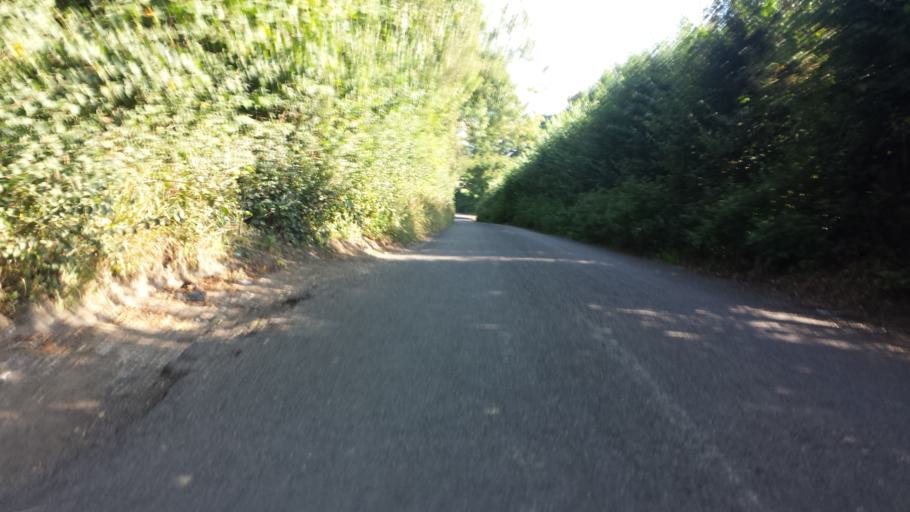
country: GB
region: England
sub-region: Kent
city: Shoreham
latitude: 51.3505
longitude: 0.1763
